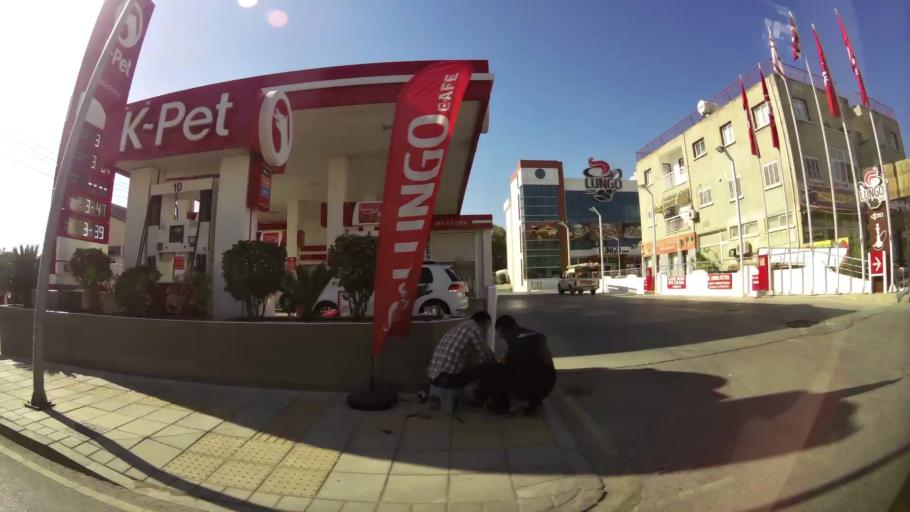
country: CY
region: Lefkosia
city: Nicosia
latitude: 35.2100
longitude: 33.3149
